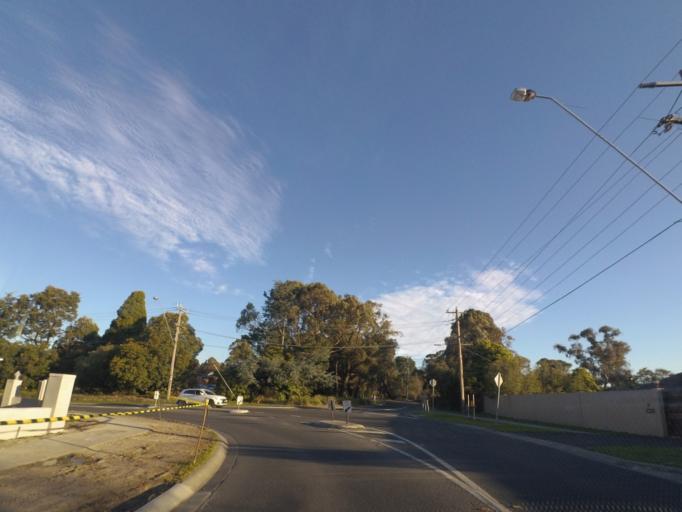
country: AU
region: Victoria
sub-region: Manningham
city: Park Orchards
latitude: -37.7834
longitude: 145.2276
